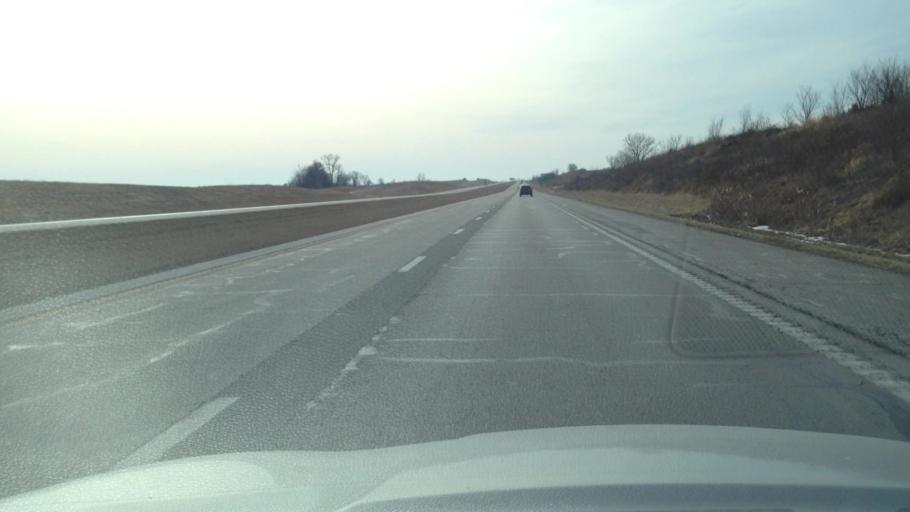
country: US
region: Missouri
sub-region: Harrison County
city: Bethany
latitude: 40.3631
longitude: -94.0063
